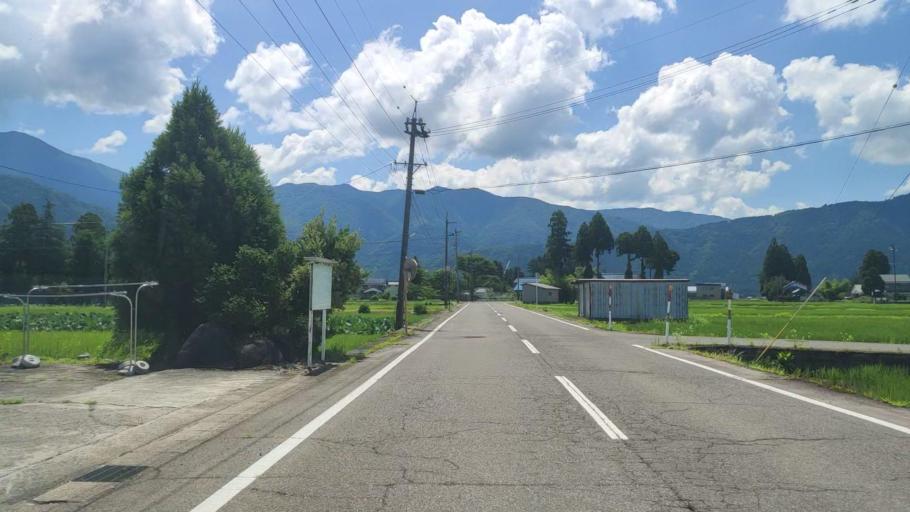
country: JP
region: Fukui
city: Ono
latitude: 35.9567
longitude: 136.5367
